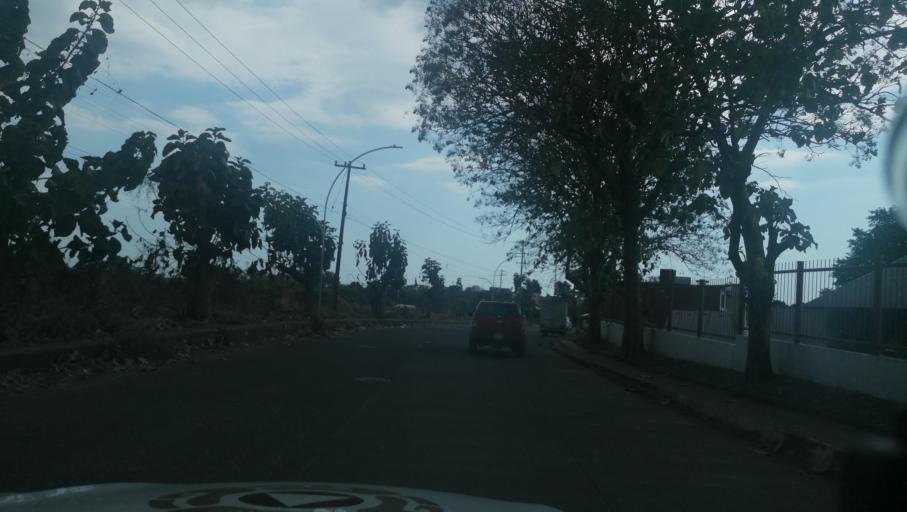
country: MX
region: Chiapas
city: Tapachula
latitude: 14.9291
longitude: -92.2518
